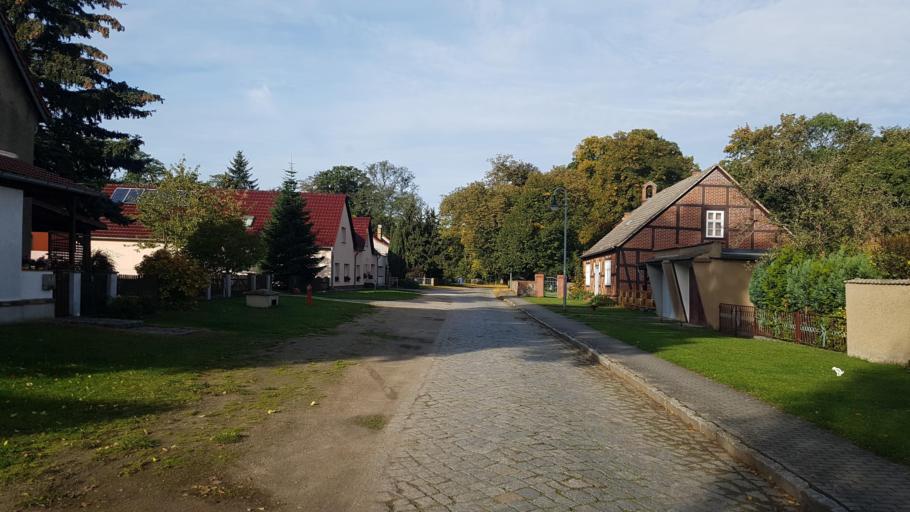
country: DE
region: Brandenburg
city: Drahnsdorf
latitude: 51.8479
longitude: 13.5282
